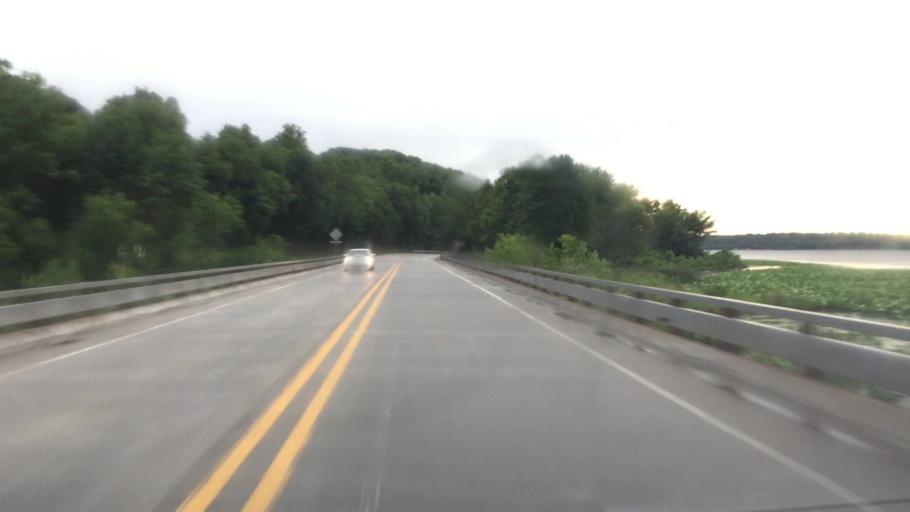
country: US
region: Iowa
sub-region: Lee County
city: Keokuk
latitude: 40.4511
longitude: -91.3694
